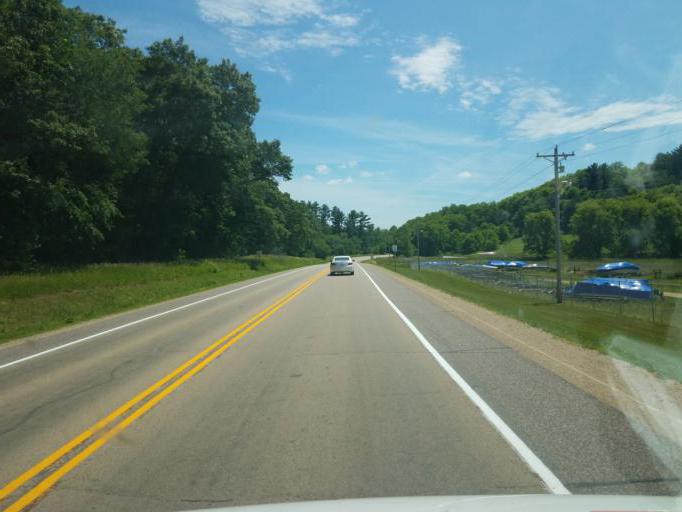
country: US
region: Wisconsin
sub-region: Sauk County
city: Reedsburg
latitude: 43.5907
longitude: -90.1262
